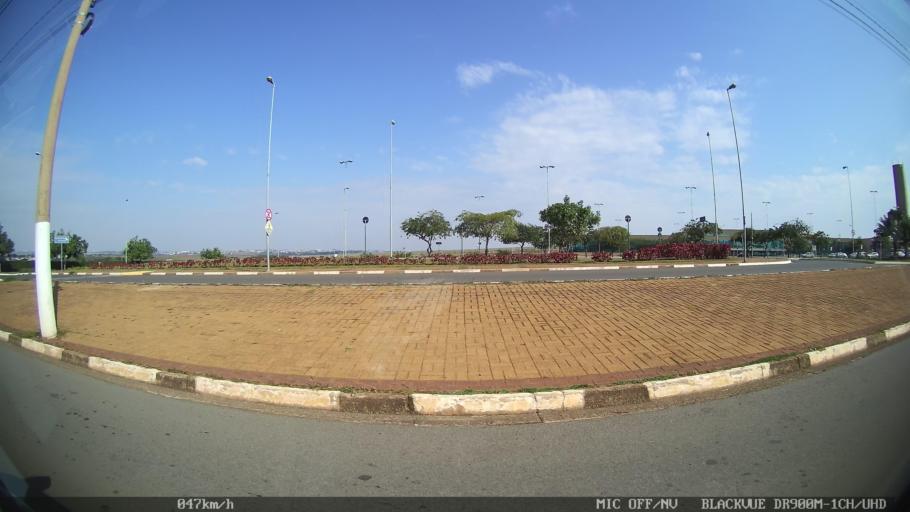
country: BR
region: Sao Paulo
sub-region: Paulinia
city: Paulinia
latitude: -22.7835
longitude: -47.1569
